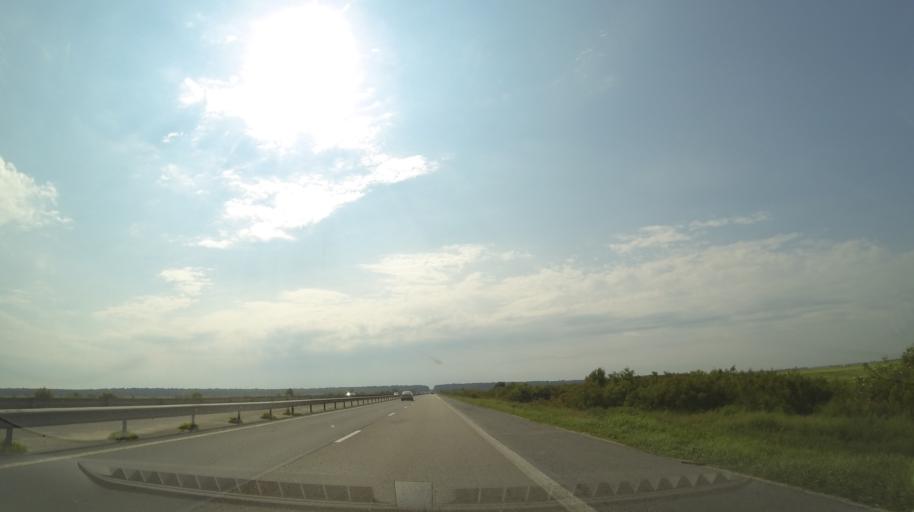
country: RO
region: Giurgiu
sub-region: Comuna Vanatorii Mici
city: Vanatorii Mici
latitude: 44.5212
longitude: 25.5503
